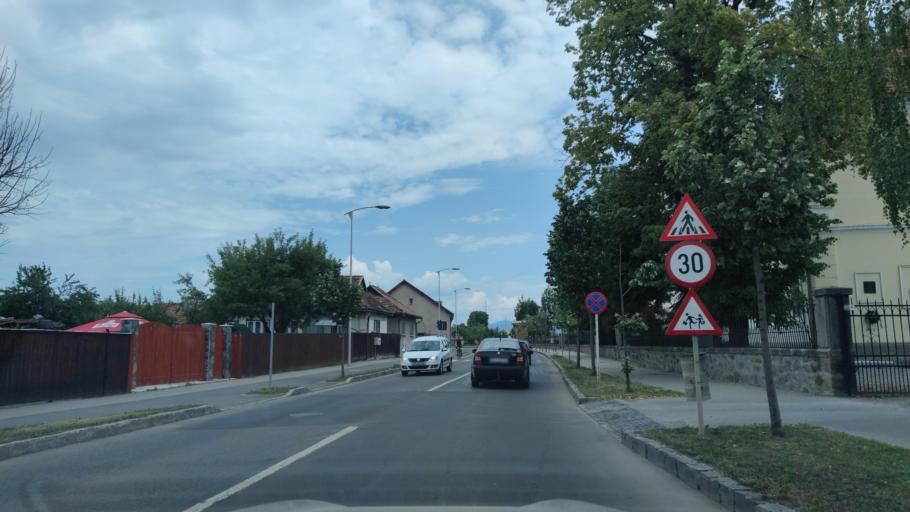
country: RO
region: Harghita
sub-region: Municipiul Miercurea Ciuc
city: Miercurea-Ciuc
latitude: 46.3774
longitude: 25.8010
